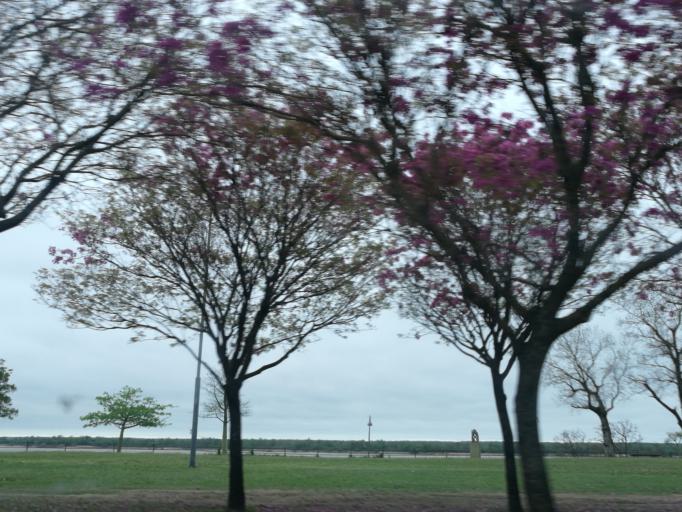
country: AR
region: Santa Fe
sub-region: Departamento de Rosario
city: Rosario
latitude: -32.9285
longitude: -60.6548
